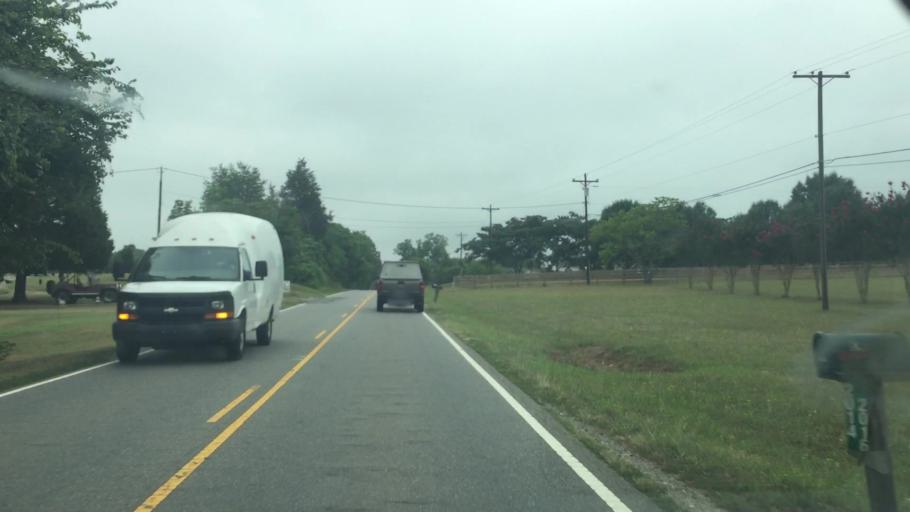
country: US
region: North Carolina
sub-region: Iredell County
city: Mooresville
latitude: 35.5259
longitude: -80.7697
